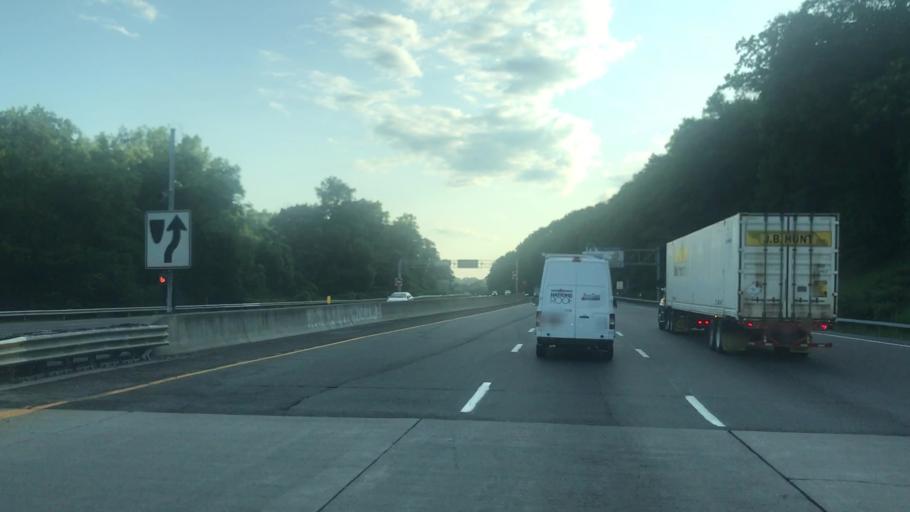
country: US
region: New York
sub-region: Westchester County
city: Hastings-on-Hudson
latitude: 40.9770
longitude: -73.8573
